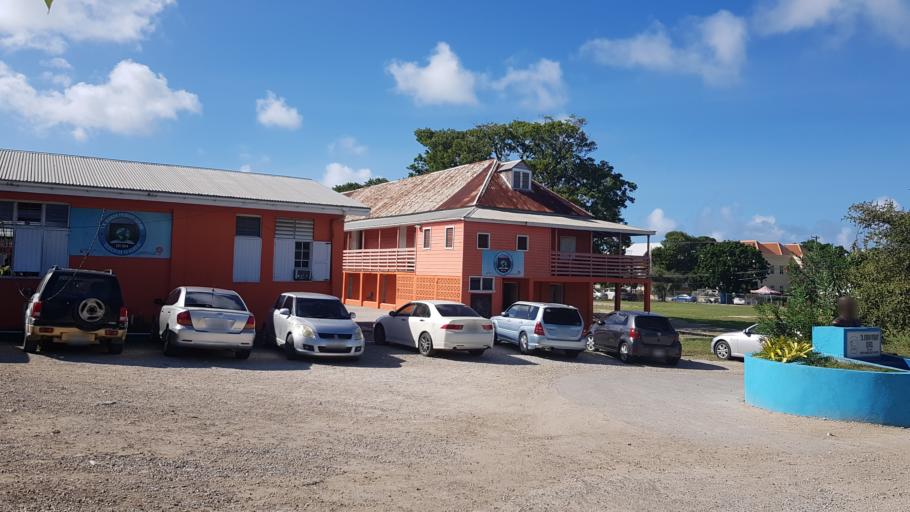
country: AG
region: Saint John
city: Saint John's
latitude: 17.1226
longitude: -61.8366
